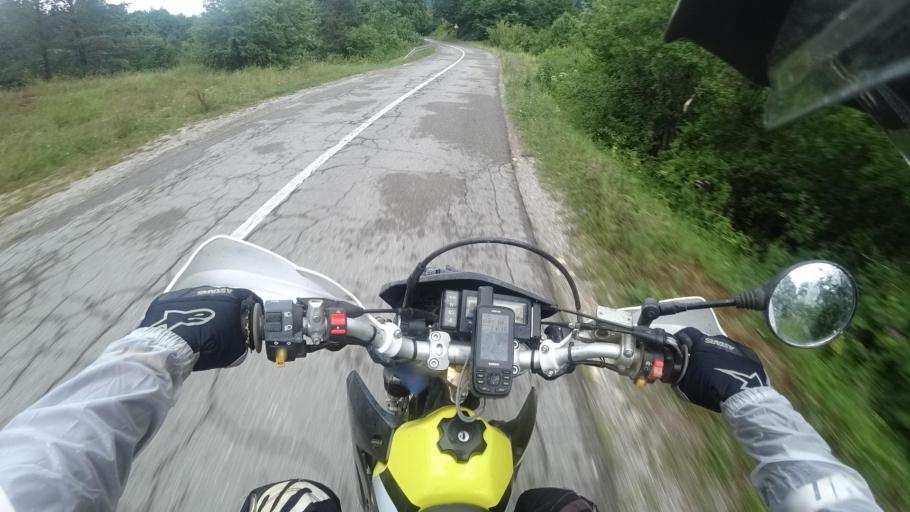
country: HR
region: Karlovacka
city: Plaski
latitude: 45.0045
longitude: 15.4268
